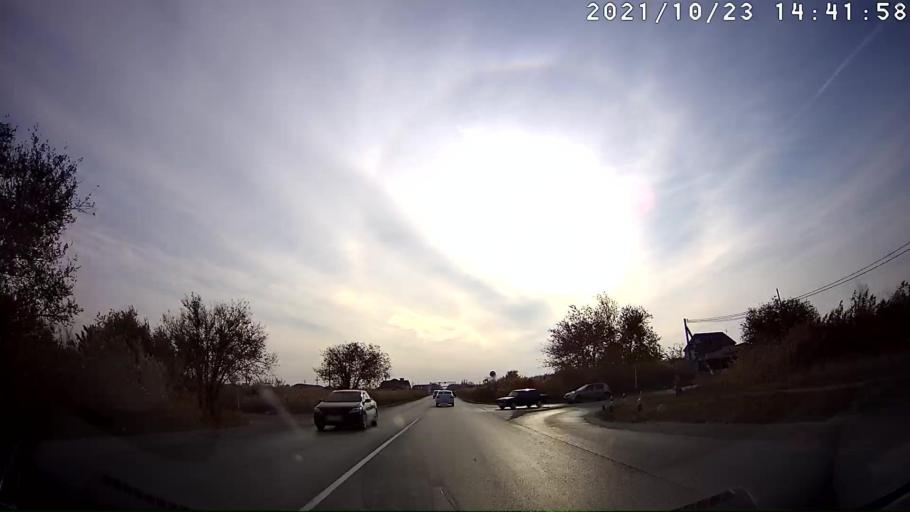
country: RU
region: Volgograd
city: Krasnoslobodsk
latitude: 48.4714
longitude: 44.5354
